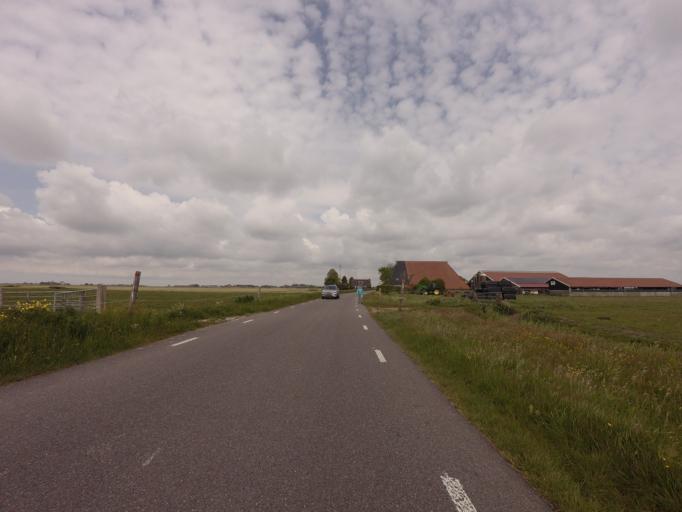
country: NL
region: Friesland
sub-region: Sudwest Fryslan
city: Bolsward
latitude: 53.0974
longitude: 5.5349
